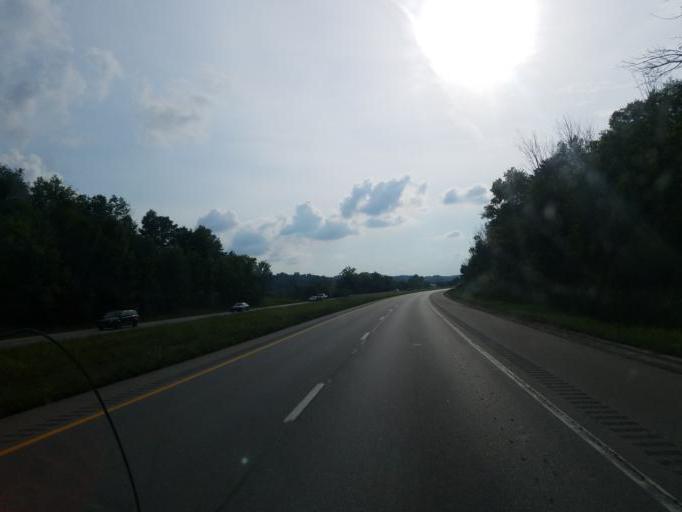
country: US
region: Ohio
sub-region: Guernsey County
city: Byesville
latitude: 40.0032
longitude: -81.5009
